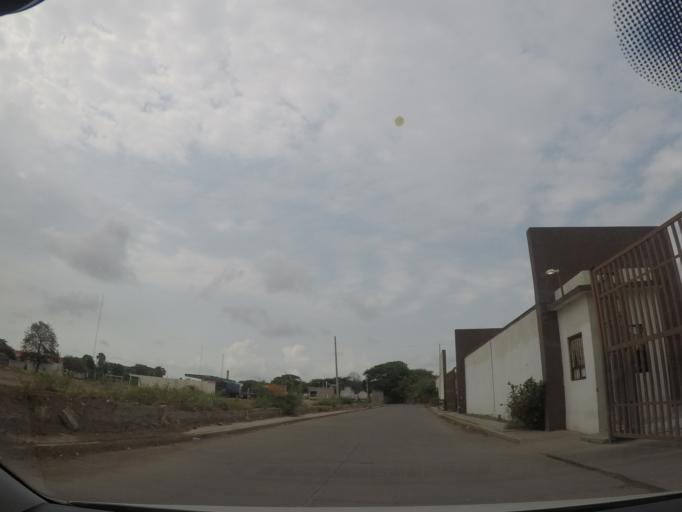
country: MX
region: Oaxaca
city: Juchitan de Zaragoza
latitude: 16.4495
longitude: -95.0148
